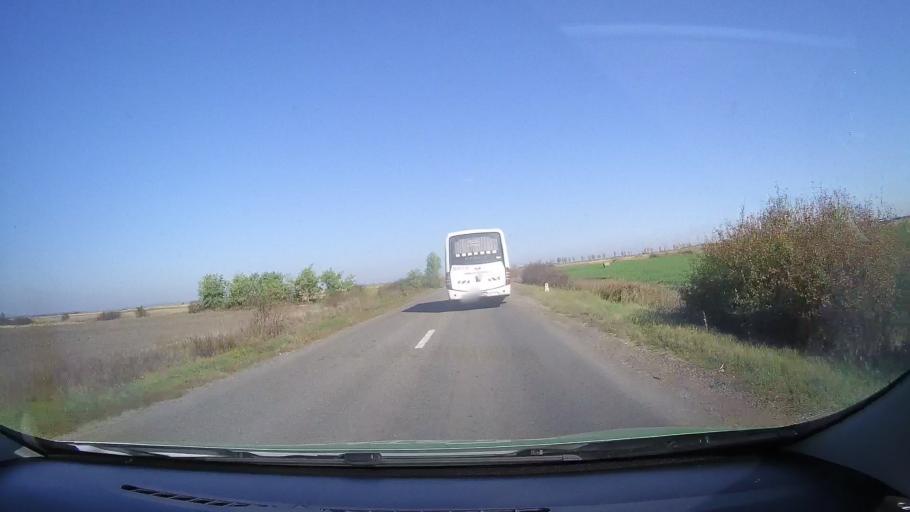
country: RO
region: Satu Mare
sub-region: Comuna Cauas
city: Cauas
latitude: 47.5864
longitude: 22.5473
